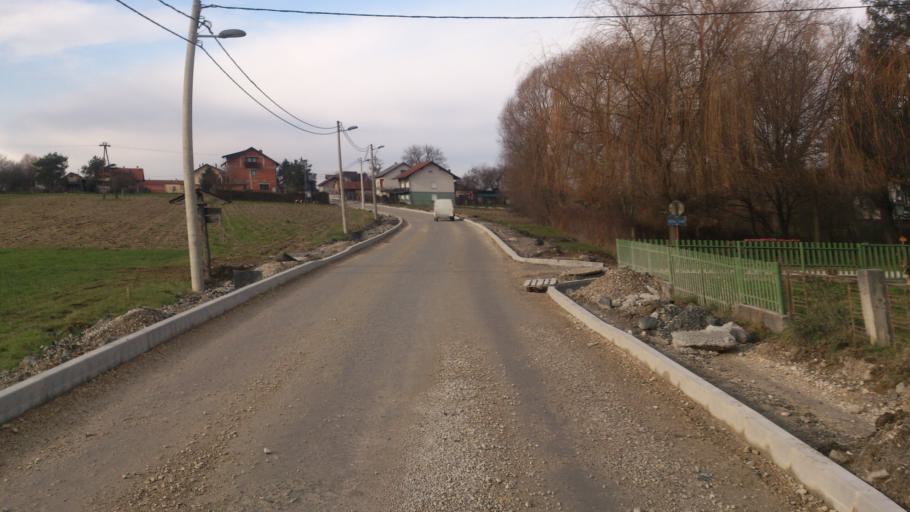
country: HR
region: Krapinsko-Zagorska
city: Marija Bistrica
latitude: 46.0500
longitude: 16.0963
